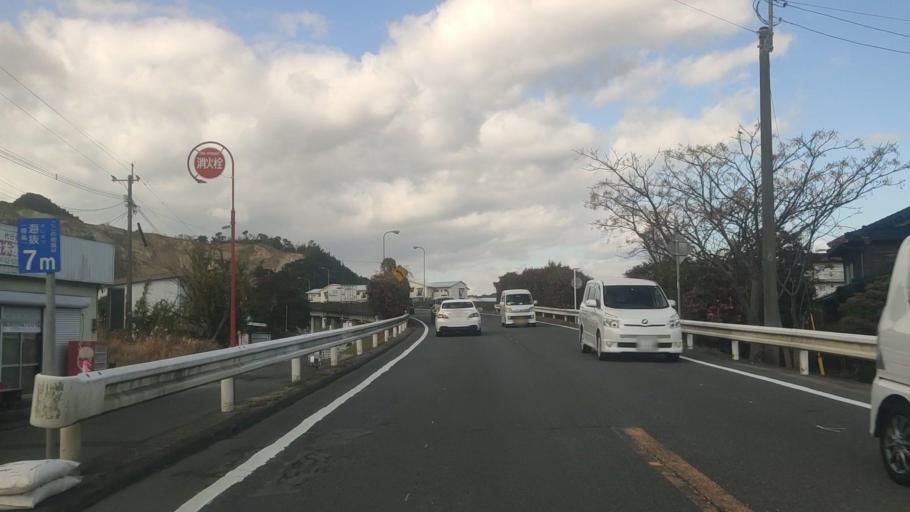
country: JP
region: Kagoshima
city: Kajiki
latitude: 31.7351
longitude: 130.6538
